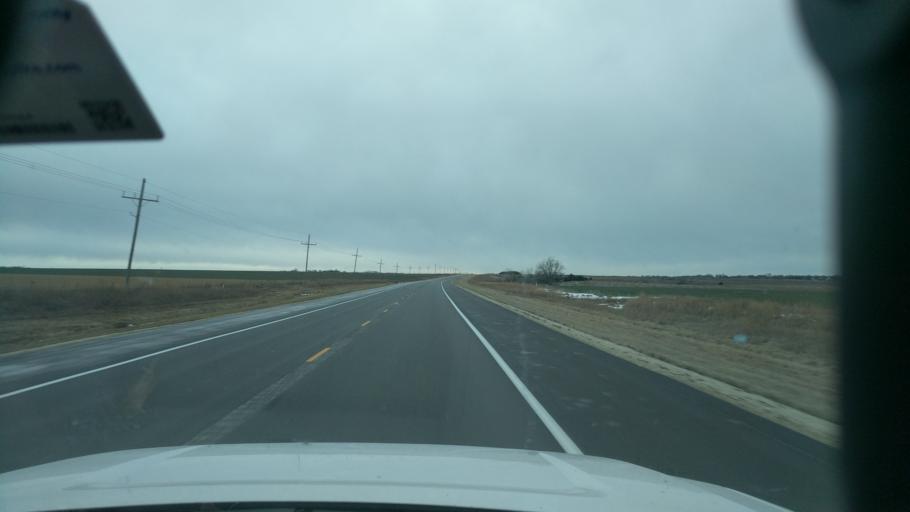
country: US
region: Kansas
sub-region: Marion County
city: Hillsboro
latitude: 38.3622
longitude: -97.2812
